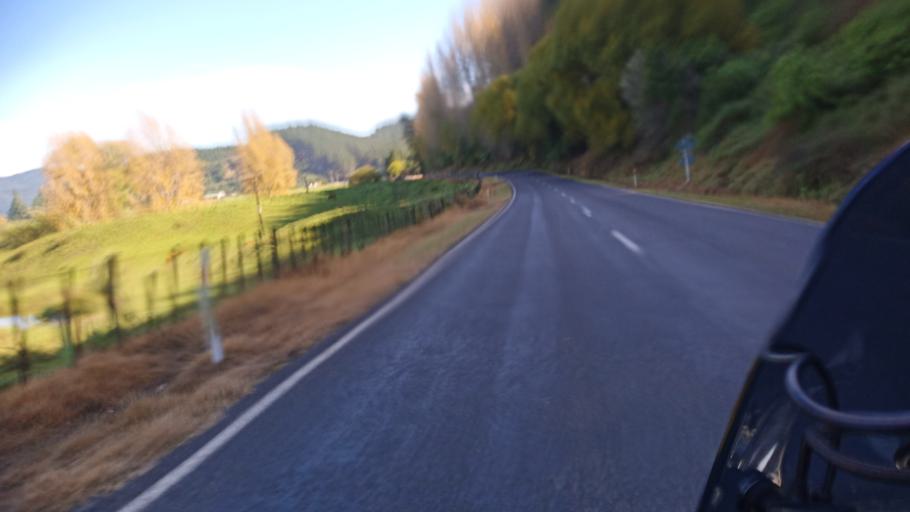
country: NZ
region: Hawke's Bay
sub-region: Wairoa District
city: Wairoa
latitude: -38.9244
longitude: 177.2716
